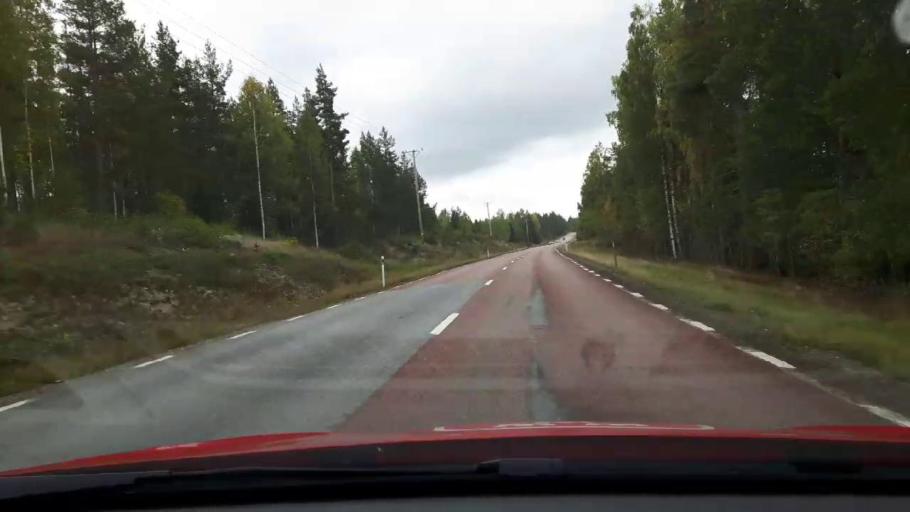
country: SE
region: Gaevleborg
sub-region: Soderhamns Kommun
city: Soderhamn
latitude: 61.1301
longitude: 16.9258
